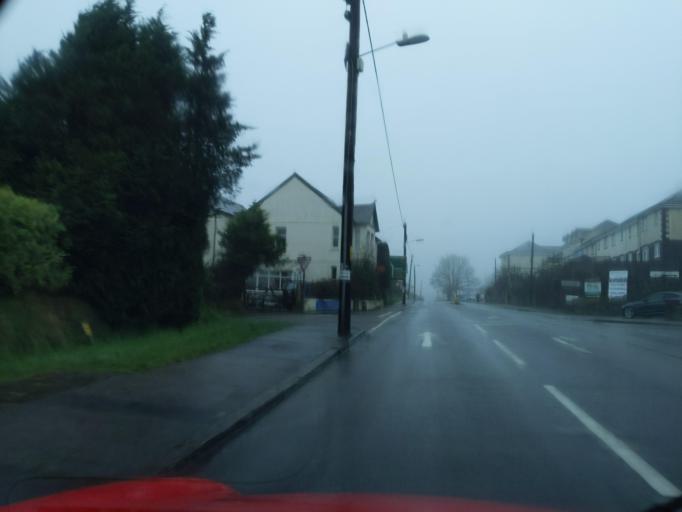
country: GB
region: England
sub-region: Cornwall
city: Callington
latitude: 50.5190
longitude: -4.3158
